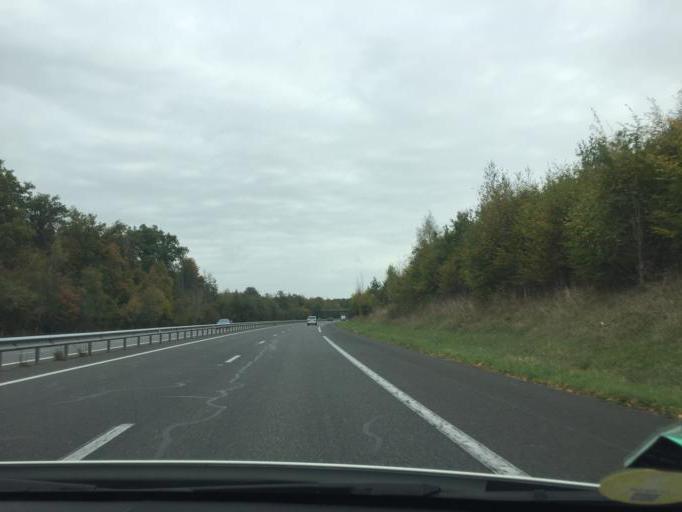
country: FR
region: Bourgogne
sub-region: Departement de l'Yonne
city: Egriselles-le-Bocage
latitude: 48.1139
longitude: 3.1345
